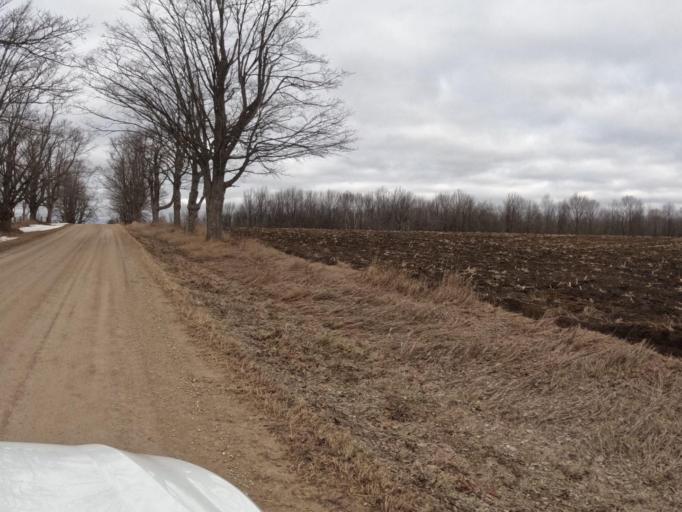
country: CA
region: Ontario
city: Shelburne
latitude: 43.8867
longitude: -80.4056
